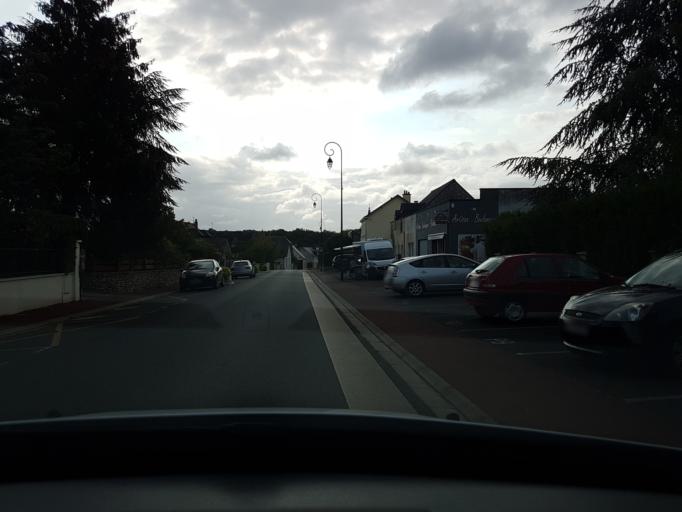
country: FR
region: Centre
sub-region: Departement d'Indre-et-Loire
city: Azay-sur-Cher
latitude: 47.3505
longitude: 0.8438
